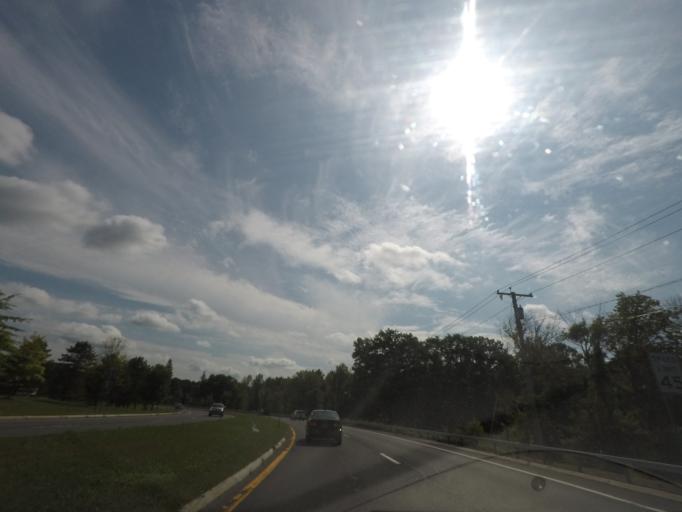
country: US
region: New York
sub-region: Albany County
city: Delmar
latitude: 42.6391
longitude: -73.8594
